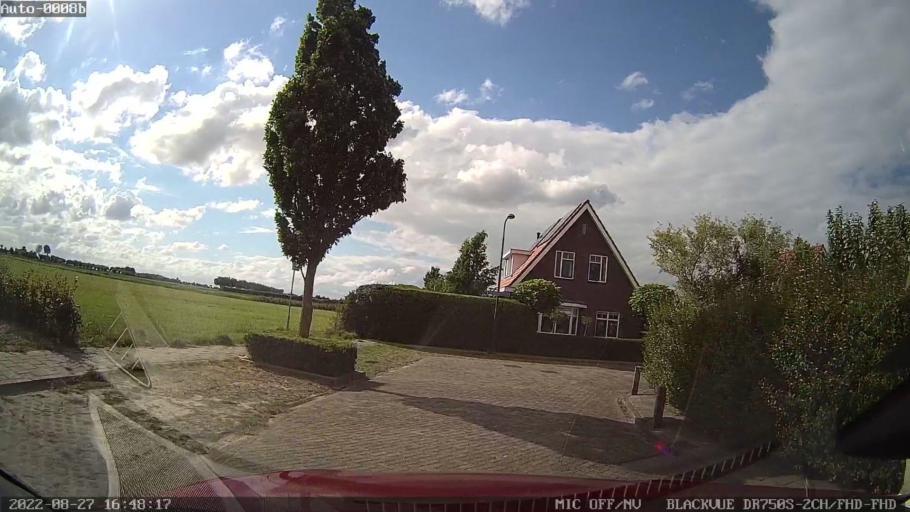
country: NL
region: South Holland
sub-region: Gemeente Goeree-Overflakkee
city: Ouddorp
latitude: 51.7101
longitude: 3.9472
